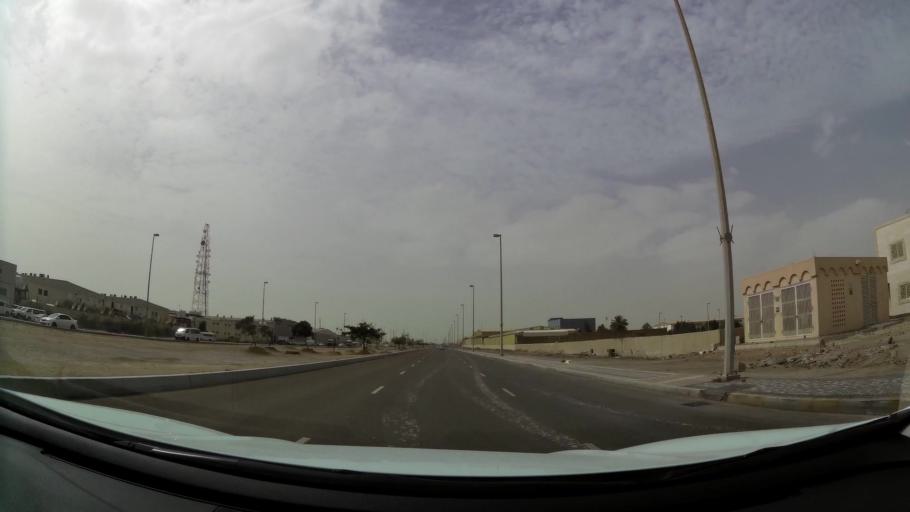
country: AE
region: Abu Dhabi
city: Abu Dhabi
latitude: 24.3679
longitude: 54.4861
